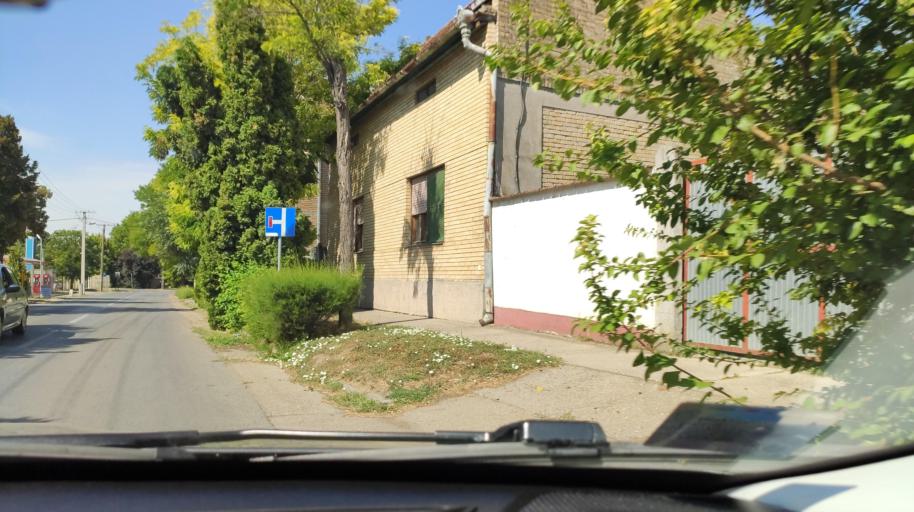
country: RS
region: Autonomna Pokrajina Vojvodina
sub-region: Severnobacki Okrug
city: Backa Topola
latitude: 45.8099
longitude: 19.6330
